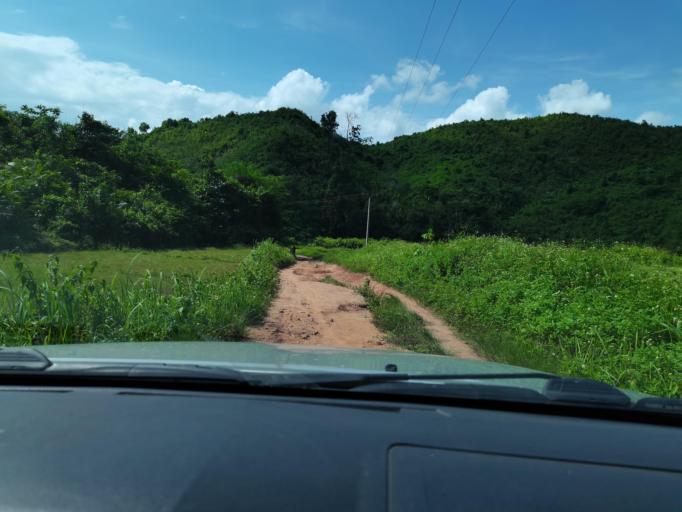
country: LA
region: Loungnamtha
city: Muang Nale
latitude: 20.5679
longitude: 101.0582
